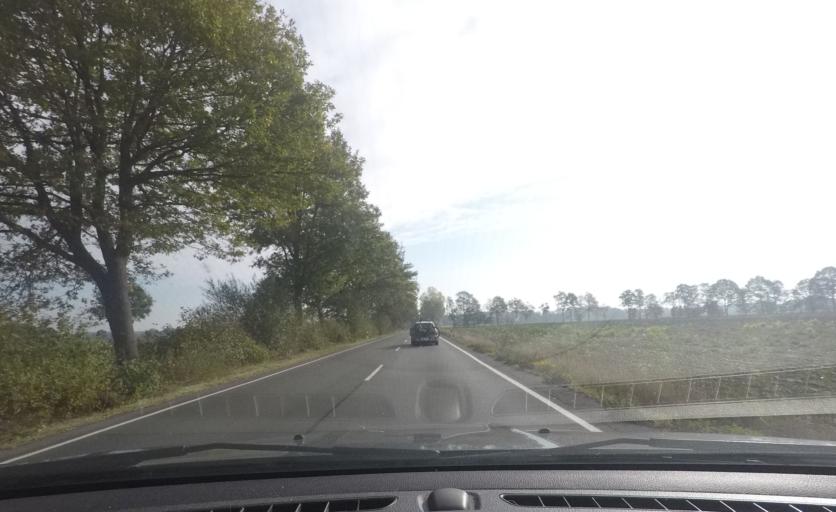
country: DE
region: North Rhine-Westphalia
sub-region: Regierungsbezirk Munster
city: Coesfeld
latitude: 51.8501
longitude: 7.1538
